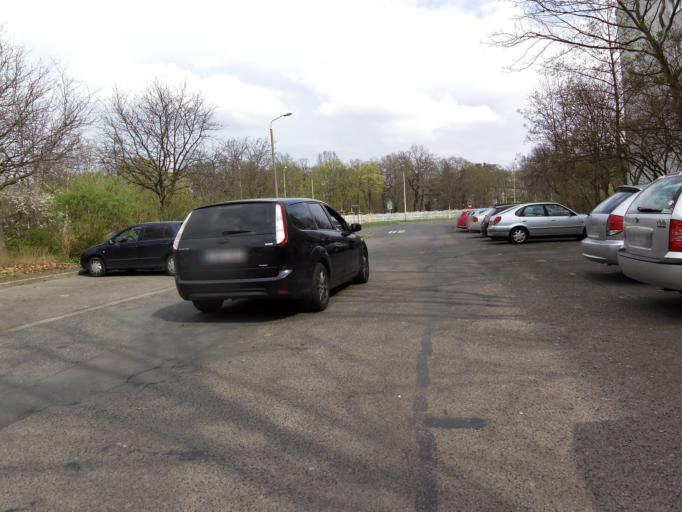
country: DE
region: Saxony
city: Markranstadt
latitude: 51.3172
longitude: 12.2957
